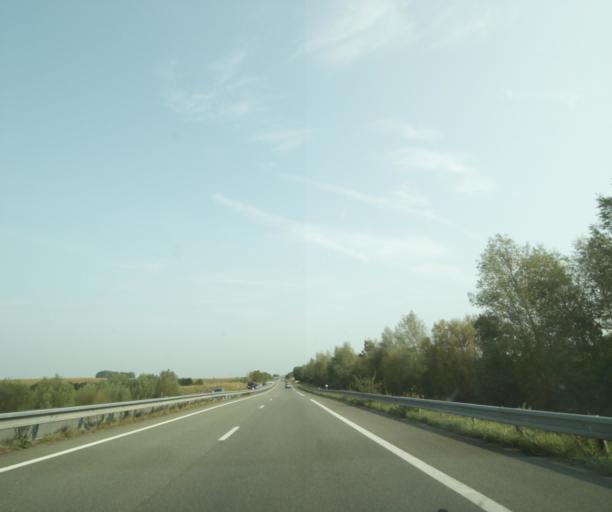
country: FR
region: Pays de la Loire
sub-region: Departement de la Sarthe
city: Sainte-Jamme-sur-Sarthe
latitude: 48.1513
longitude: 0.1433
